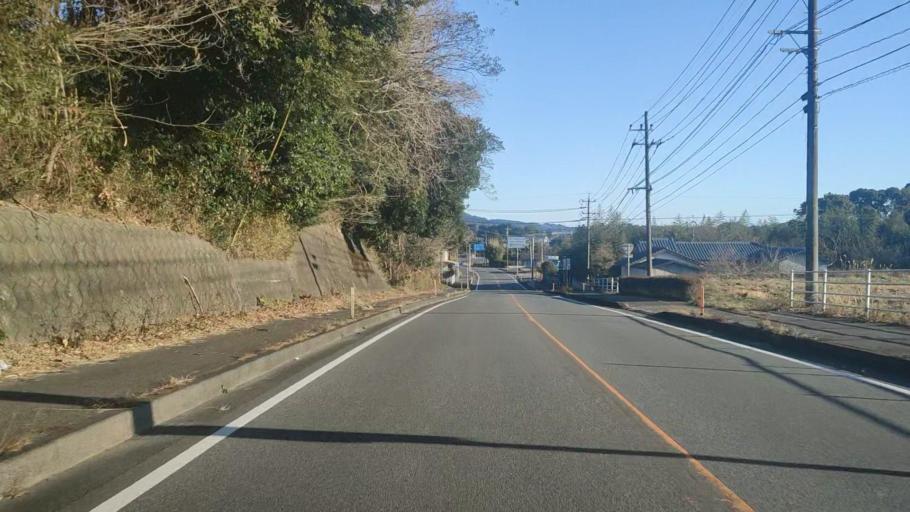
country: JP
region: Miyazaki
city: Takanabe
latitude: 32.3056
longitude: 131.5828
